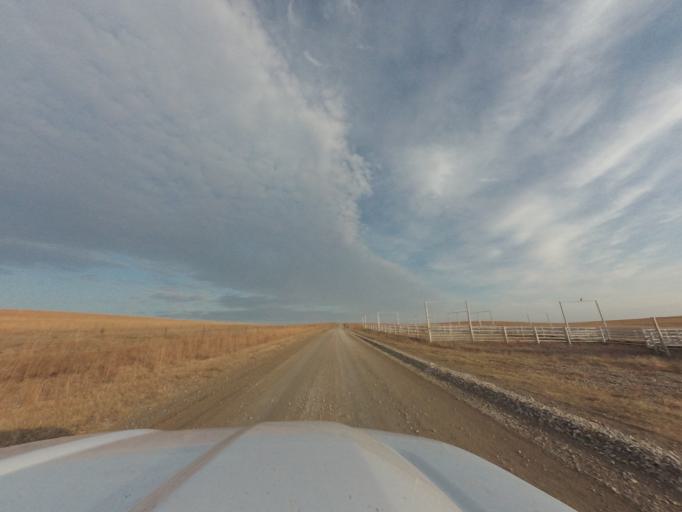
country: US
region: Kansas
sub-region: Morris County
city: Council Grove
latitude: 38.5072
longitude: -96.4101
